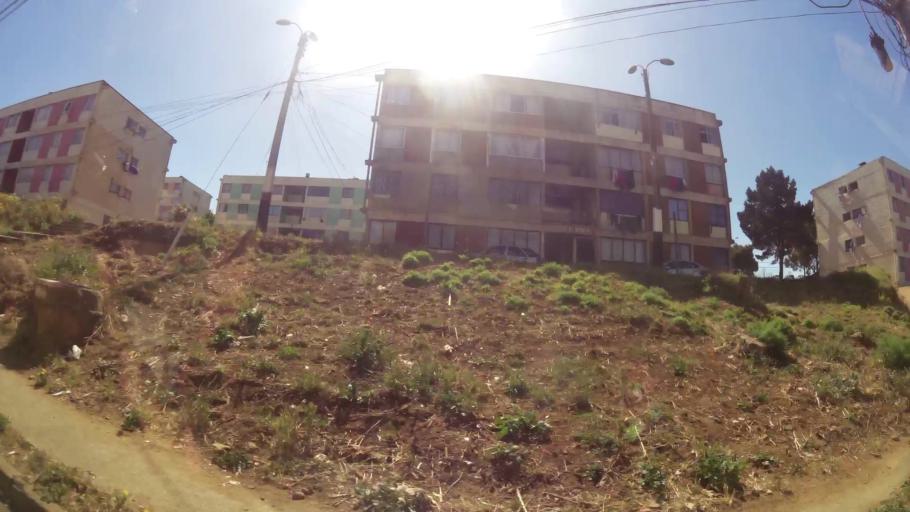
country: CL
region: Valparaiso
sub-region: Provincia de Valparaiso
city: Valparaiso
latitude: -33.0508
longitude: -71.6519
